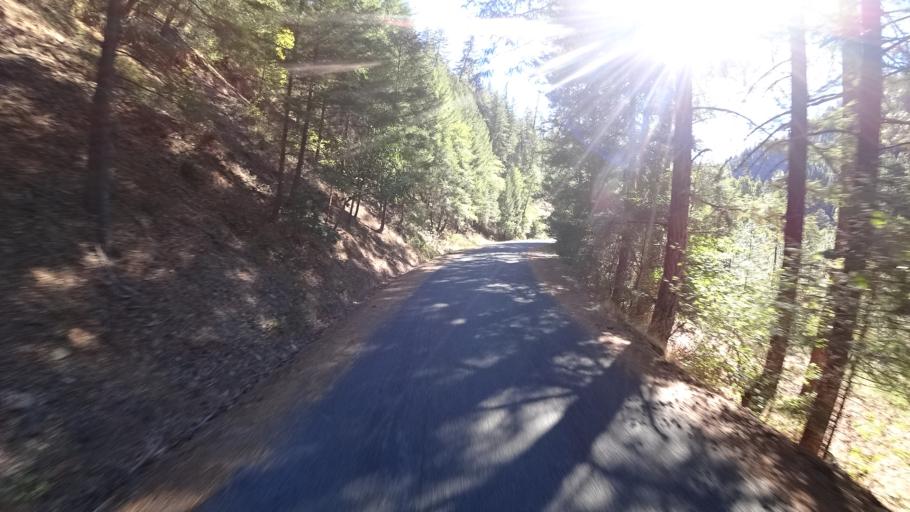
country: US
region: California
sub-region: Siskiyou County
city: Happy Camp
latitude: 41.3152
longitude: -123.1678
